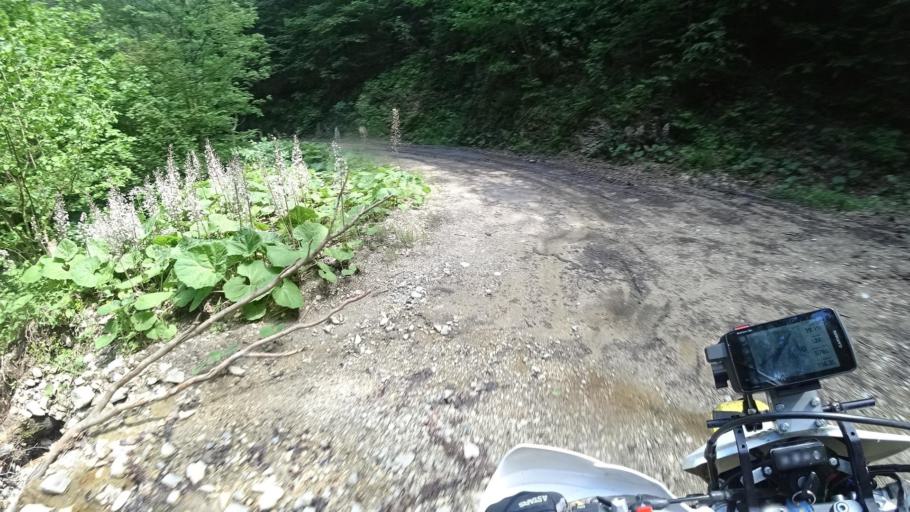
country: BA
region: Federation of Bosnia and Herzegovina
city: Orasac
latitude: 44.7385
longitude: 16.1431
